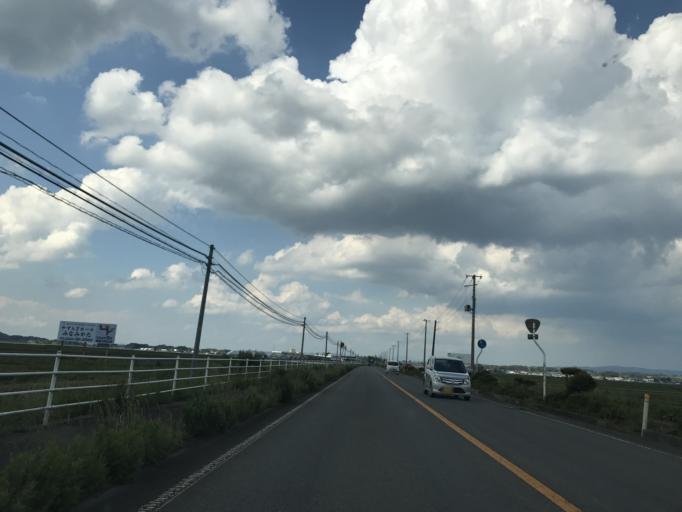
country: JP
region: Miyagi
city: Wakuya
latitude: 38.6212
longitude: 141.1833
